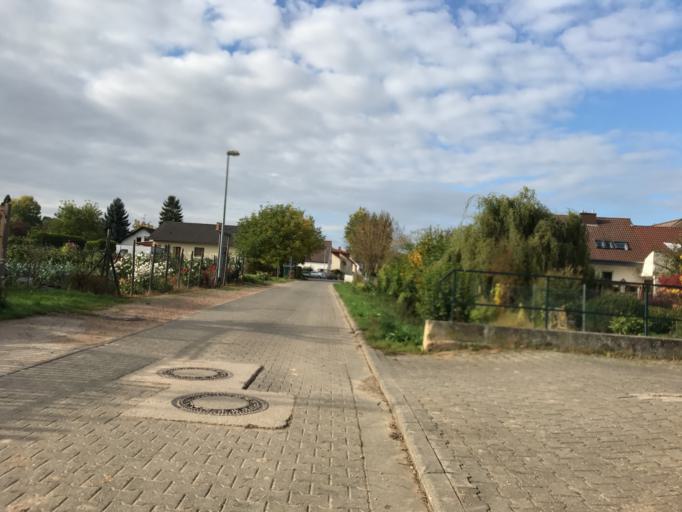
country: DE
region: Rheinland-Pfalz
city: Appenheim
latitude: 49.9305
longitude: 8.0370
